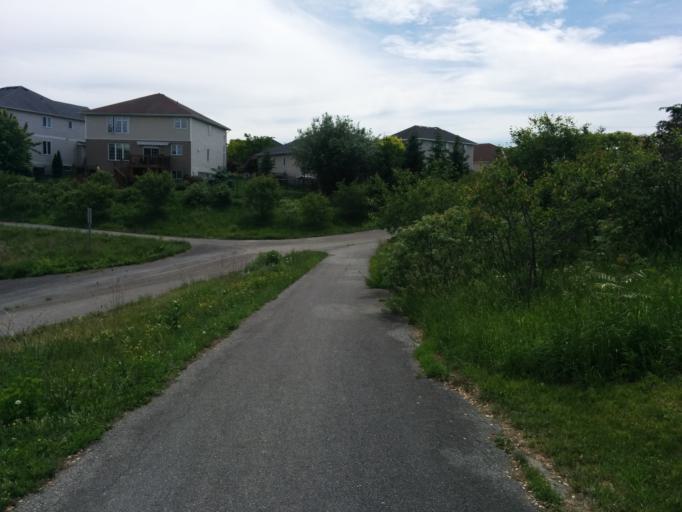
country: CA
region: Ontario
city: Clarence-Rockland
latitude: 45.4831
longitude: -75.4637
